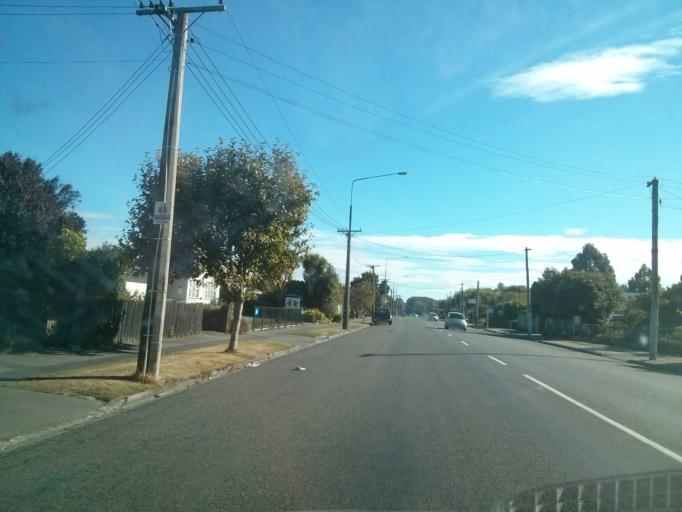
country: NZ
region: Canterbury
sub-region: Christchurch City
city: Christchurch
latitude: -43.4934
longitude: 172.5645
